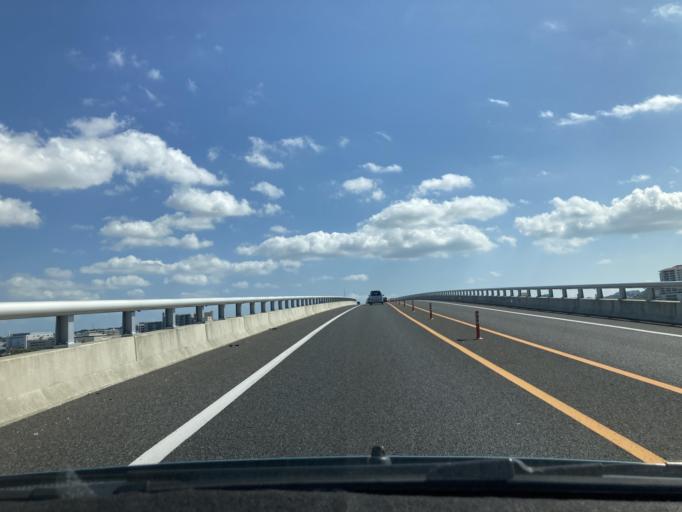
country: JP
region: Okinawa
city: Ginowan
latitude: 26.2732
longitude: 127.7201
